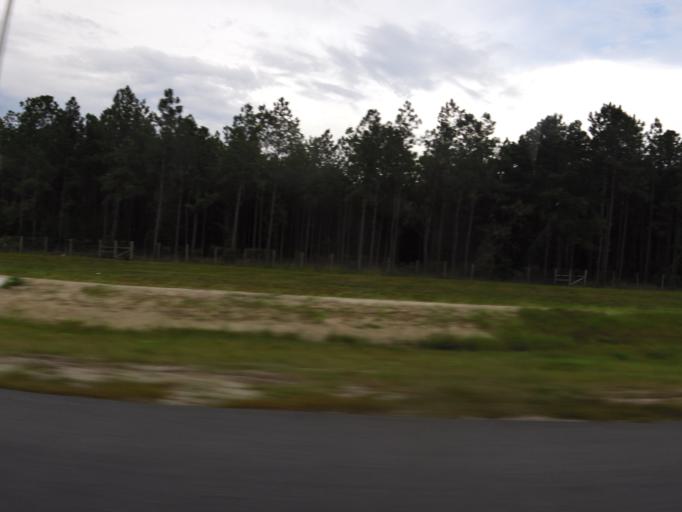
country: US
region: Florida
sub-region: Clay County
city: Lakeside
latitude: 30.1852
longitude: -81.8365
